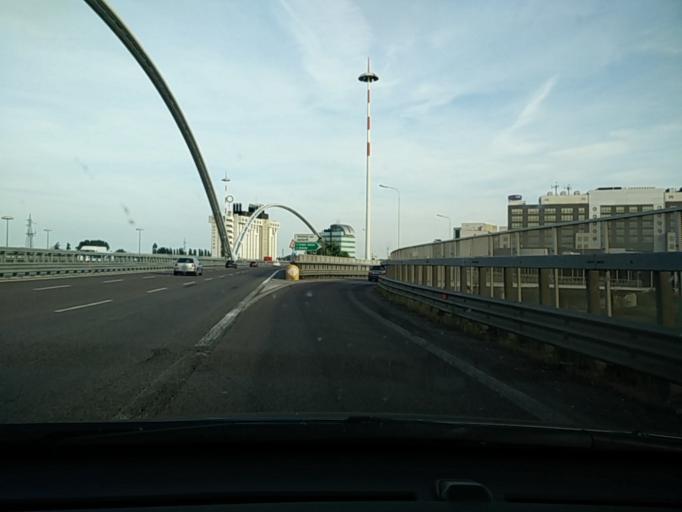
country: IT
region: Veneto
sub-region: Provincia di Padova
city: Noventa
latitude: 45.4184
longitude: 11.9301
